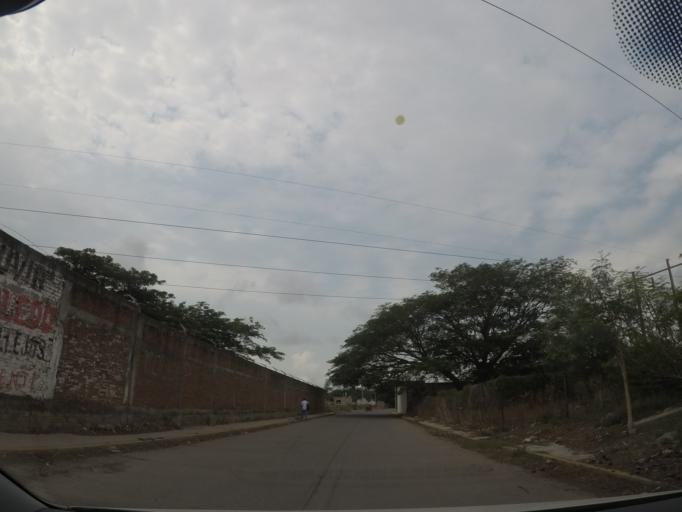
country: MX
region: Oaxaca
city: Juchitan de Zaragoza
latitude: 16.4501
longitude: -95.0147
